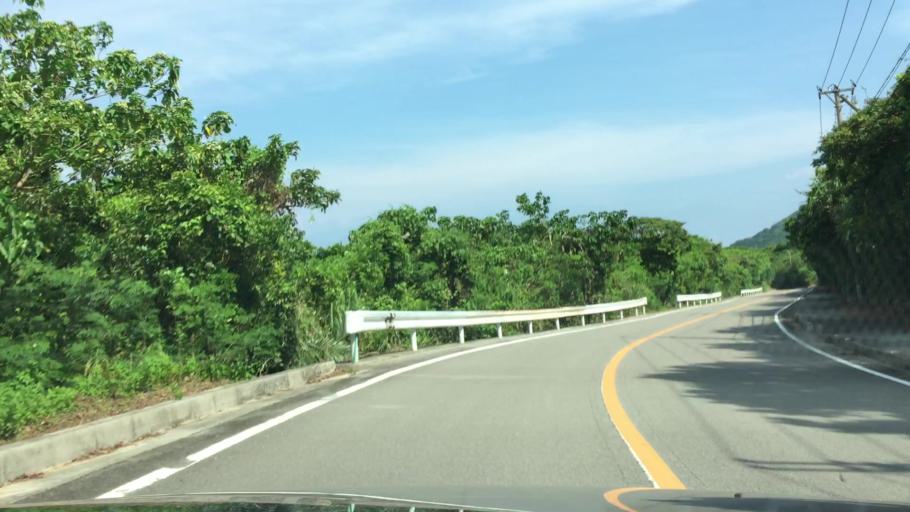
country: JP
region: Okinawa
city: Ishigaki
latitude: 24.5119
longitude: 124.2670
